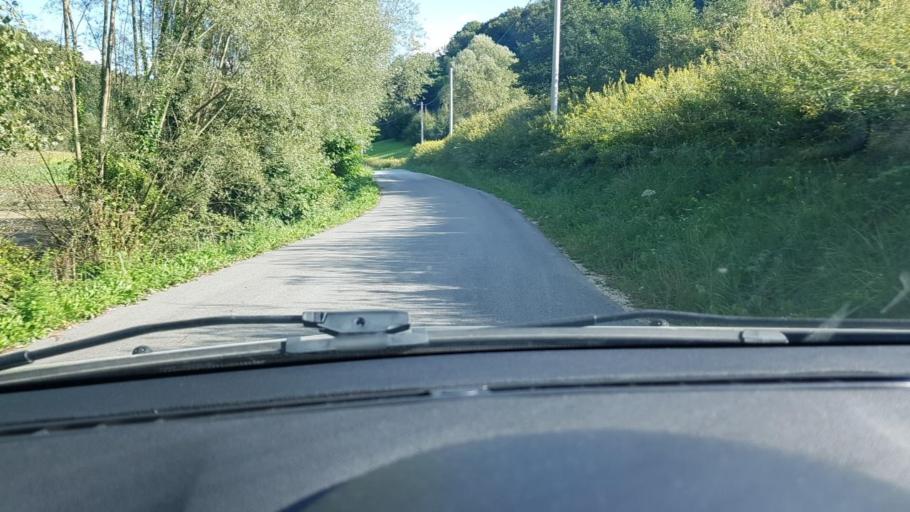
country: HR
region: Krapinsko-Zagorska
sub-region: Grad Krapina
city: Krapina
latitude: 46.1365
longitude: 15.8375
